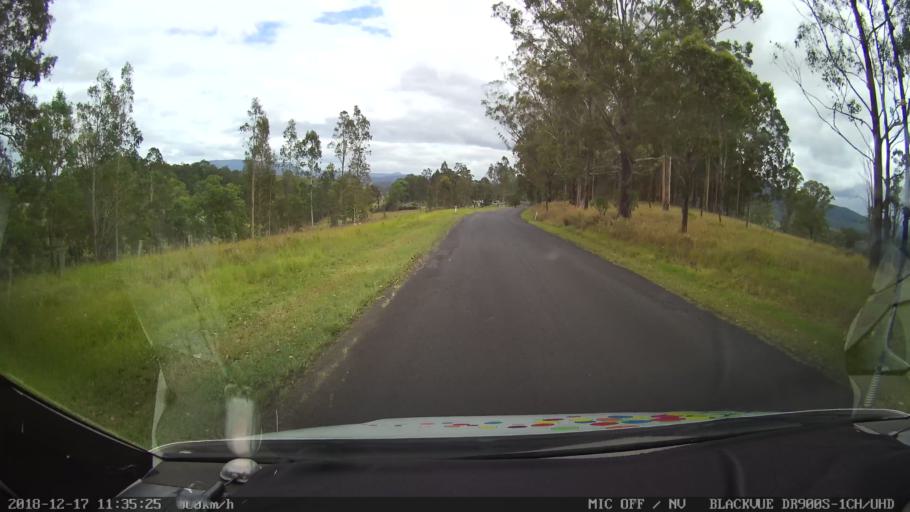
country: AU
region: New South Wales
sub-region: Kyogle
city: Kyogle
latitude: -28.7229
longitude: 152.6066
